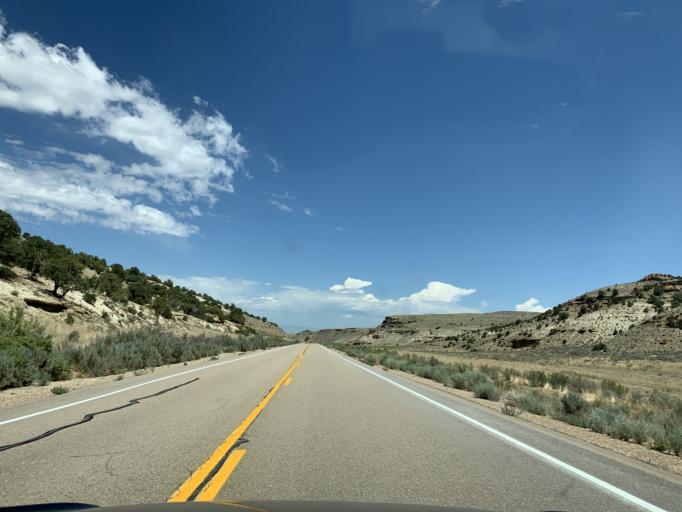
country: US
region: Utah
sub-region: Duchesne County
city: Duchesne
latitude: 39.9923
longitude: -110.1555
